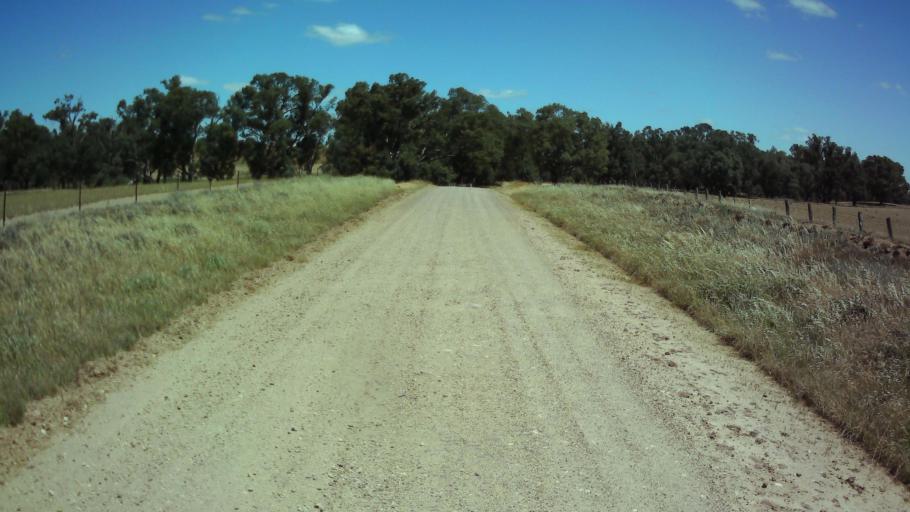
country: AU
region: New South Wales
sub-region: Weddin
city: Grenfell
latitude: -33.9315
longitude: 148.3344
